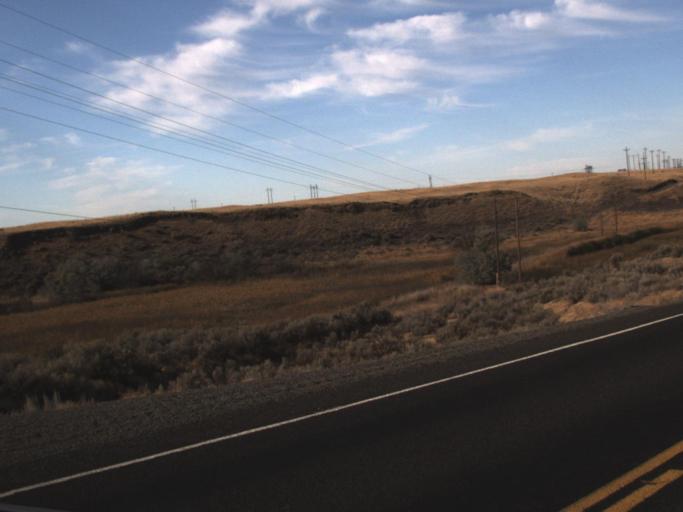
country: US
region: Washington
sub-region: Franklin County
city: Connell
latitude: 46.6642
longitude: -118.9948
